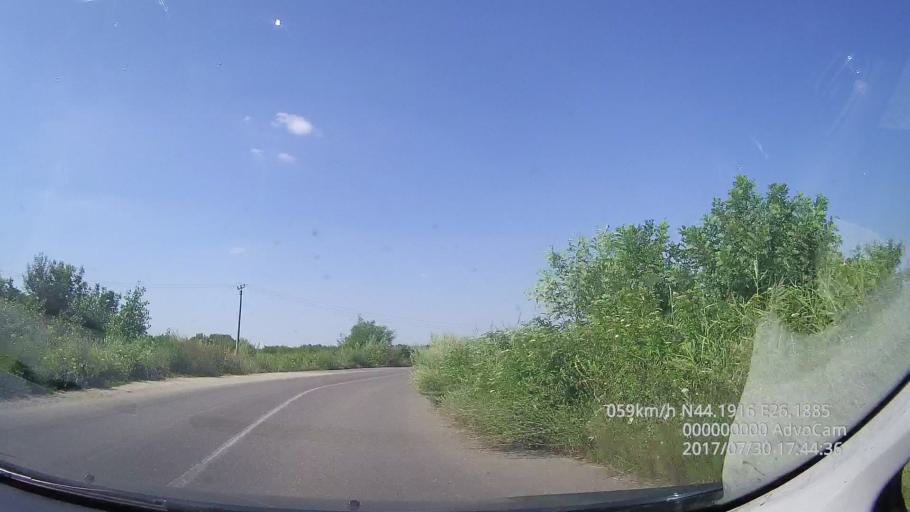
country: RO
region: Giurgiu
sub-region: Comuna Comana
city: Falastoaca
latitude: 44.1919
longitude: 26.1885
